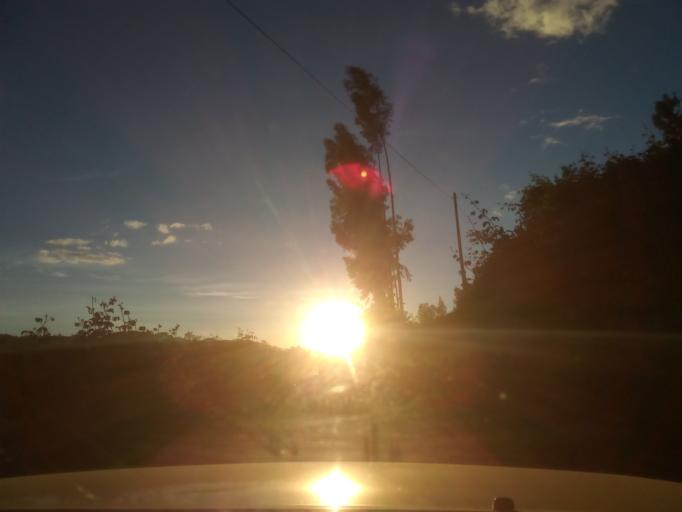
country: PE
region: La Libertad
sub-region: Provincia de Otuzco
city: Mache
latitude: -8.0492
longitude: -78.4559
